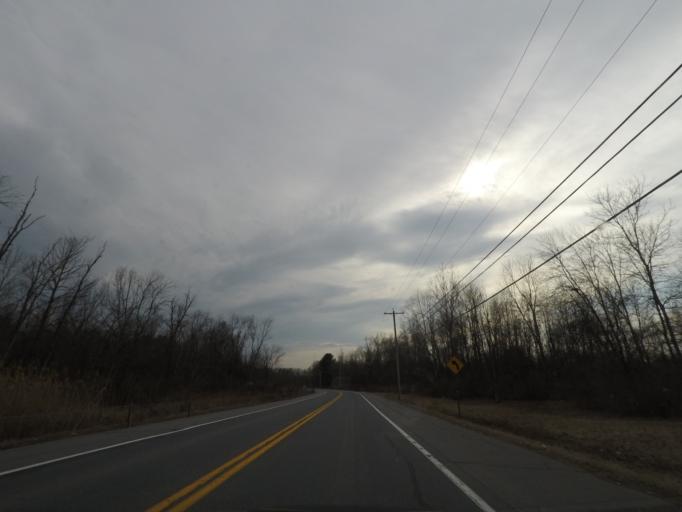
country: US
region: New York
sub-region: Saratoga County
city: Schuylerville
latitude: 43.1432
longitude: -73.5827
